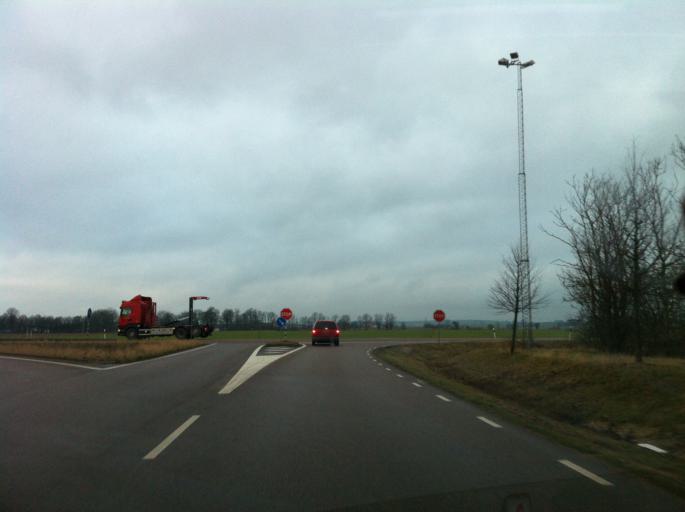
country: SE
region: Skane
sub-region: Landskrona
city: Asmundtorp
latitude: 55.8748
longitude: 12.8878
